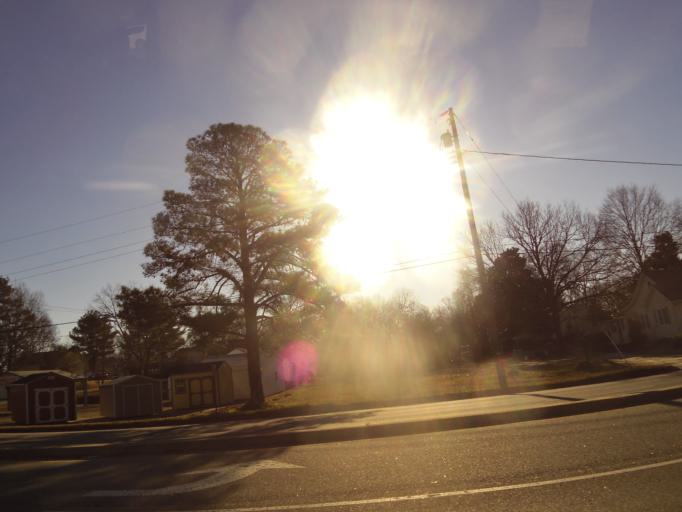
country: US
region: Virginia
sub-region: City of Hopewell
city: Hopewell
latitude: 37.2817
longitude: -77.3047
